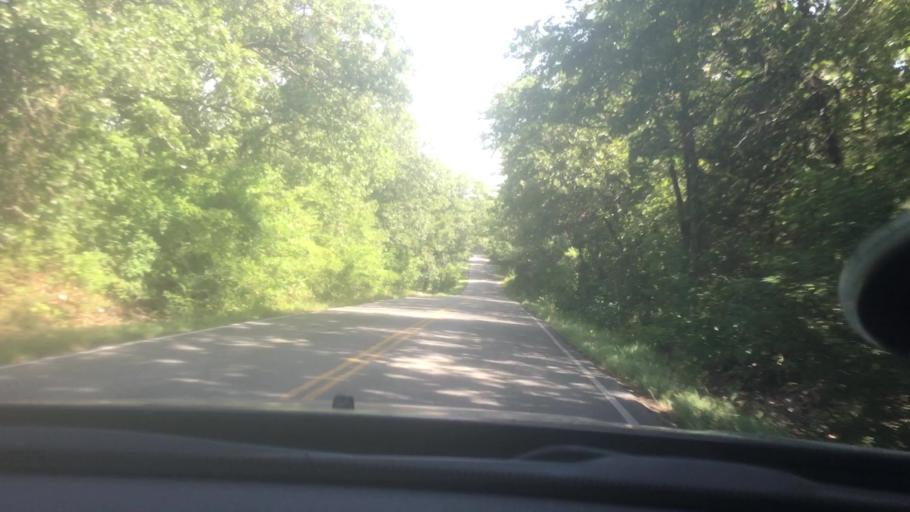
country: US
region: Oklahoma
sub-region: Bryan County
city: Durant
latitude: 34.0454
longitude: -96.4742
